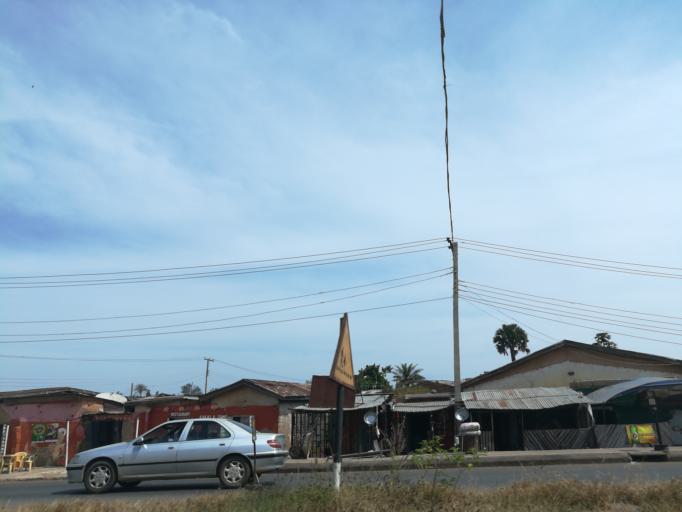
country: NG
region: Plateau
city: Bukuru
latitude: 9.8004
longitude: 8.8595
